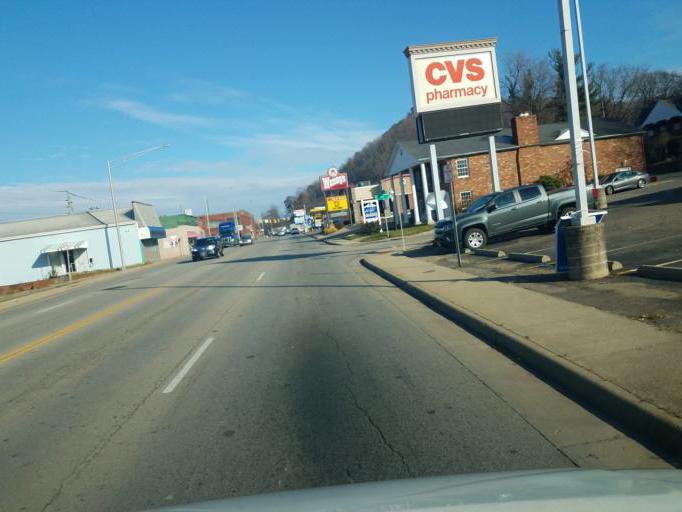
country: US
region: Ohio
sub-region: Scioto County
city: Portsmouth
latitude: 38.7576
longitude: -82.9909
